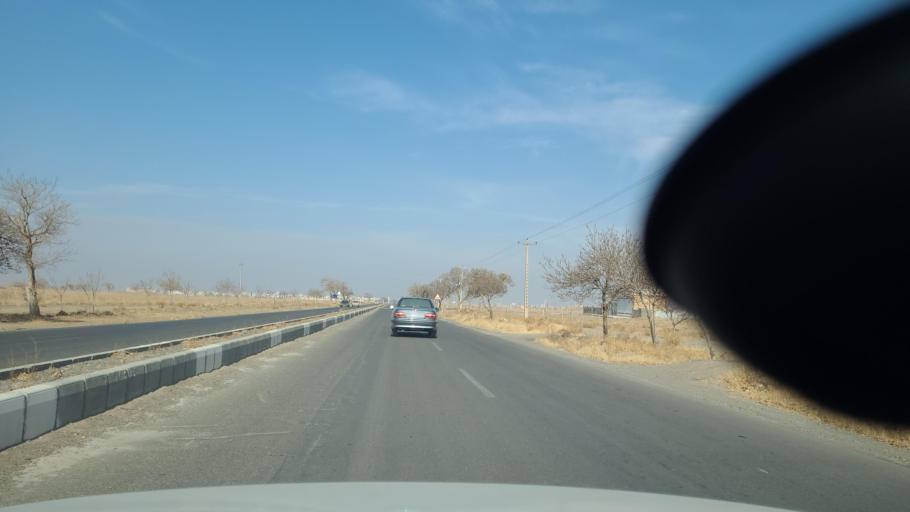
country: IR
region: Razavi Khorasan
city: Fariman
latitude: 35.6674
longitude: 59.8418
